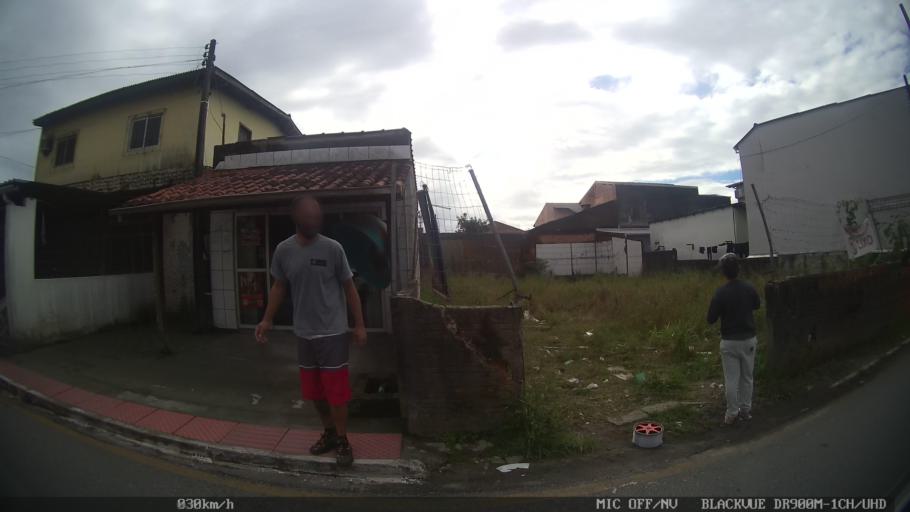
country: BR
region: Santa Catarina
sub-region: Sao Jose
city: Campinas
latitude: -27.5775
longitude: -48.6205
